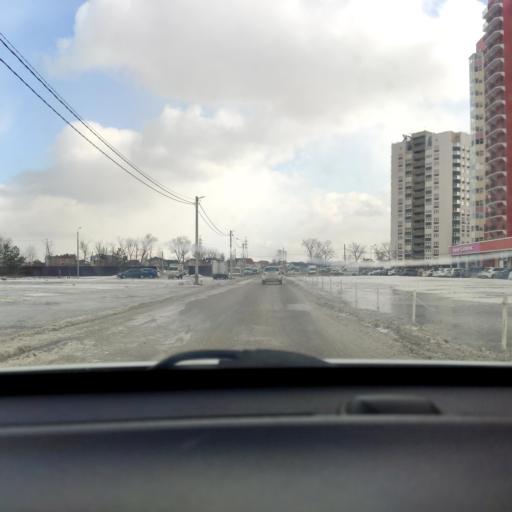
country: RU
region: Voronezj
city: Somovo
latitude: 51.6717
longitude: 39.3201
